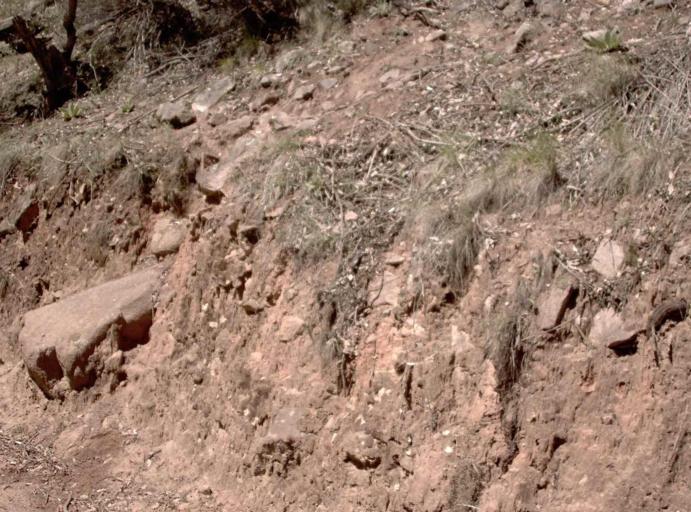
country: AU
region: New South Wales
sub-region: Snowy River
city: Jindabyne
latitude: -37.0471
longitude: 148.5401
